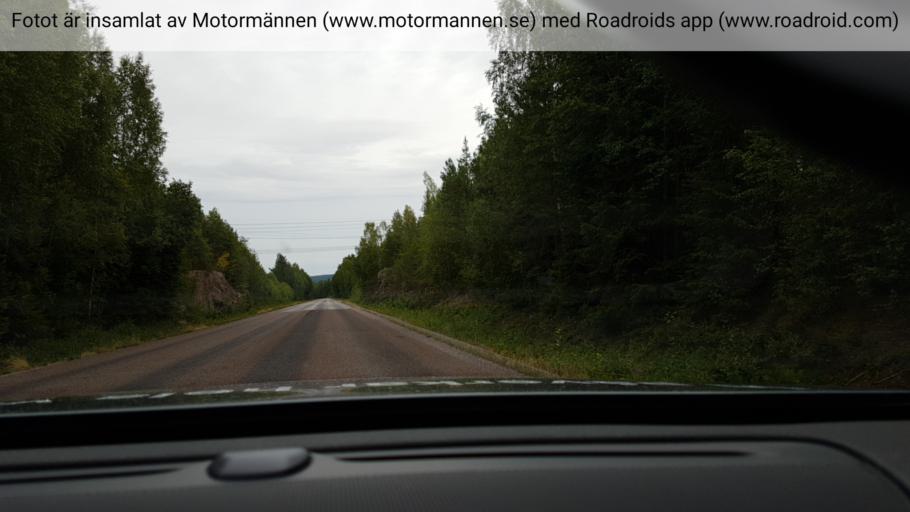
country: SE
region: Dalarna
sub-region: Ludvika Kommun
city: Ludvika
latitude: 60.2943
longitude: 15.2252
